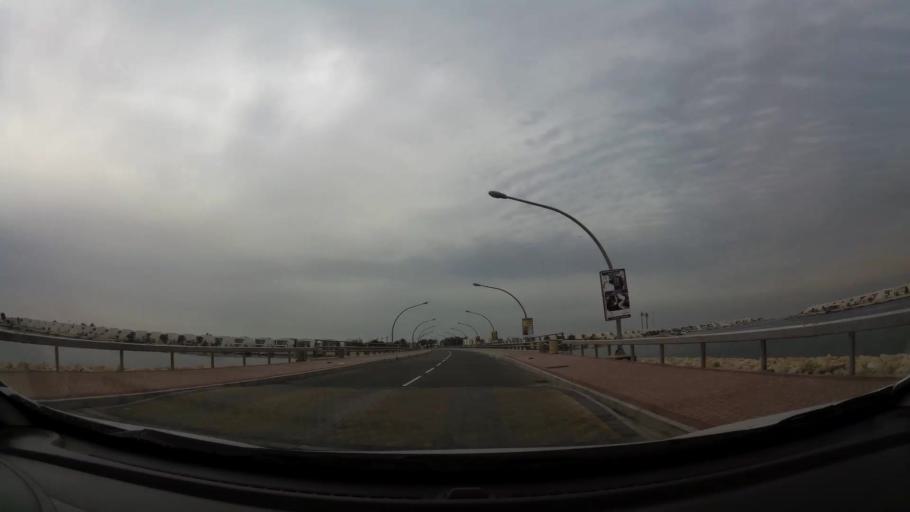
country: BH
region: Central Governorate
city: Dar Kulayb
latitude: 25.8353
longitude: 50.6148
